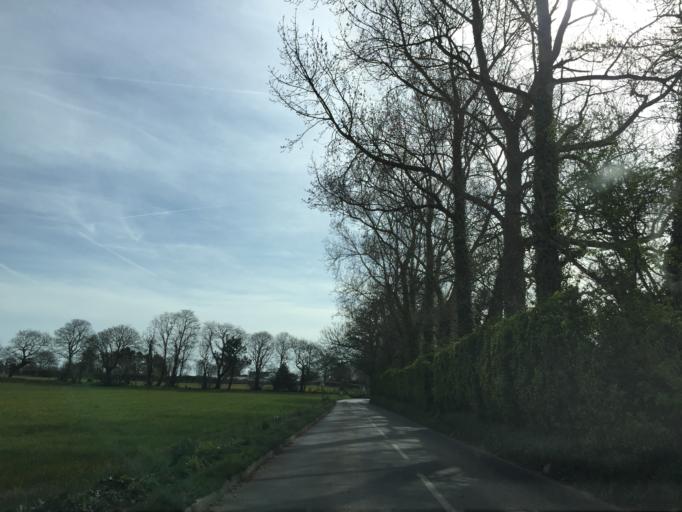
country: JE
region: St Helier
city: Saint Helier
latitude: 49.2289
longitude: -2.0711
